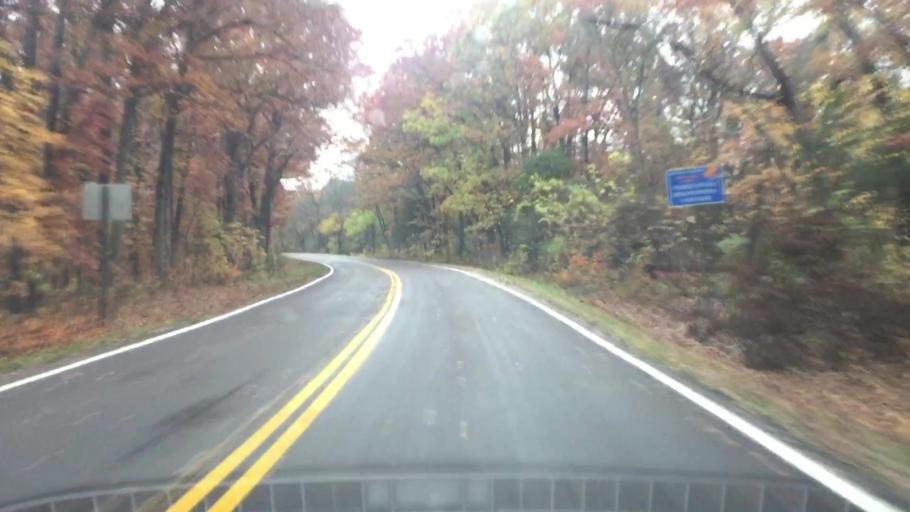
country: US
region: Missouri
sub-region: Boone County
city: Columbia
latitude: 38.8688
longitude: -92.3185
